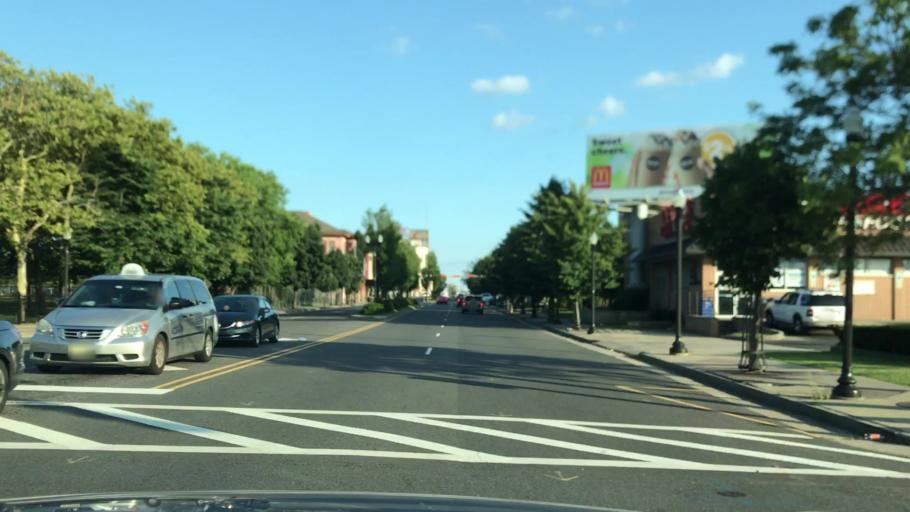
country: US
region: New Jersey
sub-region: Atlantic County
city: Atlantic City
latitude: 39.3634
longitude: -74.4339
